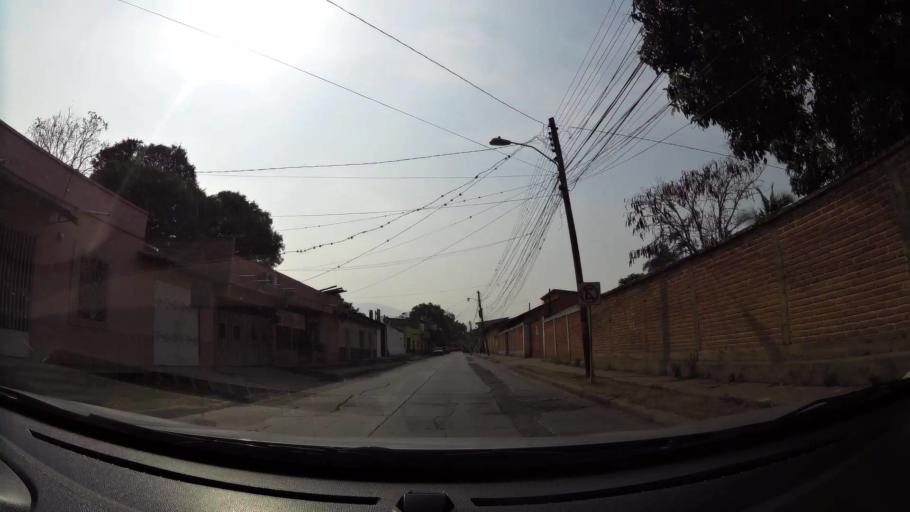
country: HN
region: Comayagua
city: Comayagua
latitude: 14.4637
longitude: -87.6454
